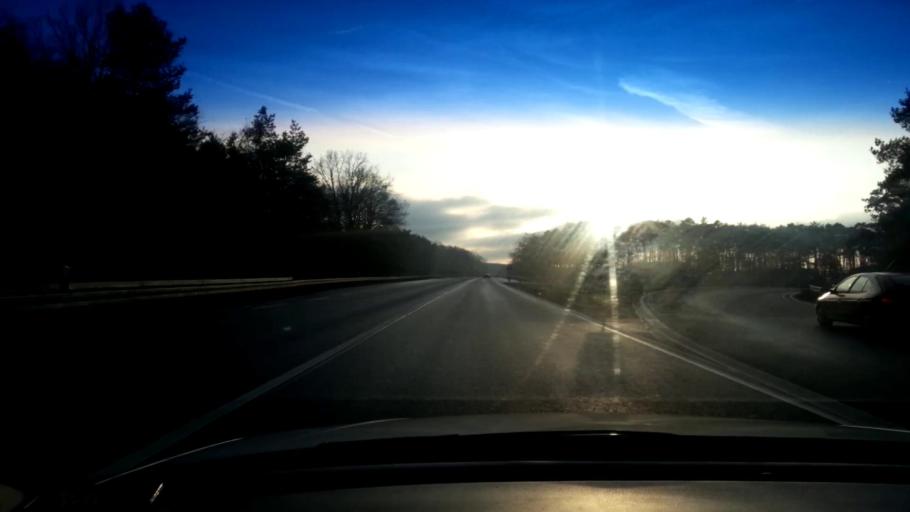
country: DE
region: Bavaria
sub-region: Upper Franconia
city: Hirschaid
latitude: 49.8056
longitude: 10.9590
